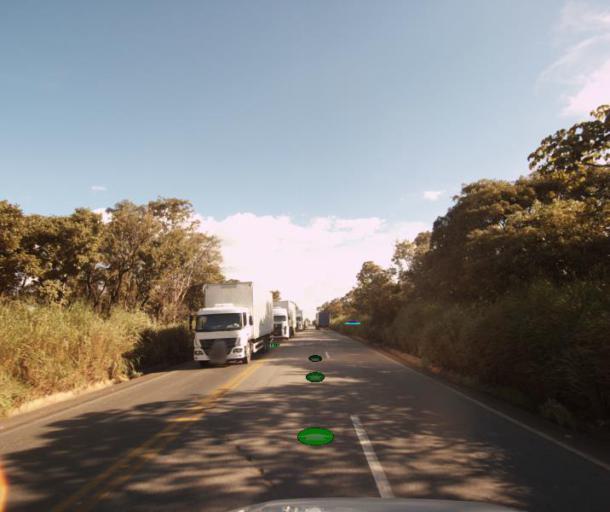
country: BR
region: Goias
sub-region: Porangatu
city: Porangatu
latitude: -13.0948
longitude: -49.1956
